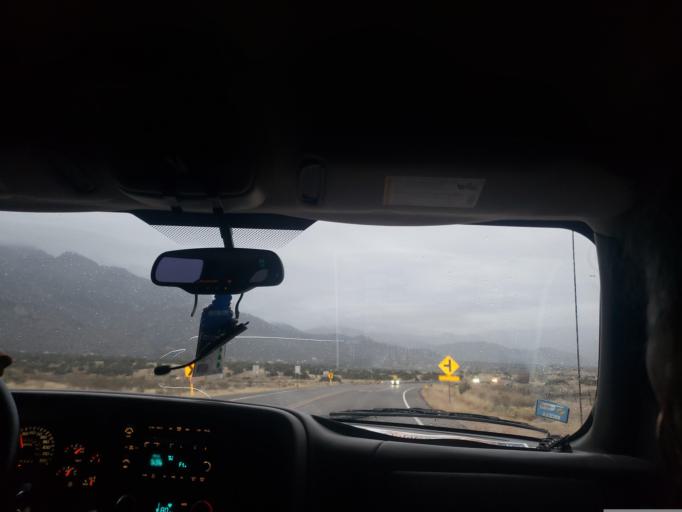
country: US
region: New Mexico
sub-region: Bernalillo County
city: Sandia Heights
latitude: 35.2009
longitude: -106.5074
